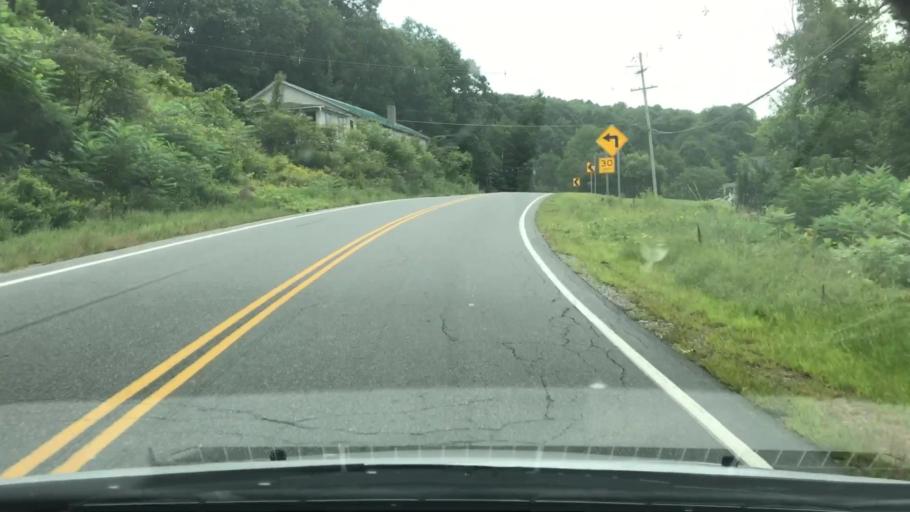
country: US
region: New Hampshire
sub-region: Grafton County
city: Woodsville
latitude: 44.1332
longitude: -72.0313
